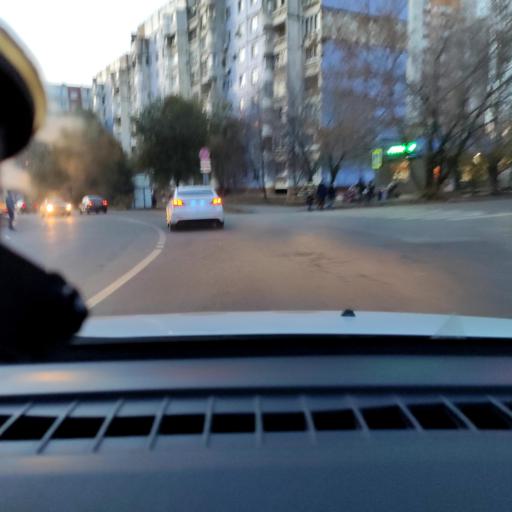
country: RU
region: Samara
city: Samara
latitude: 53.2433
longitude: 50.1969
